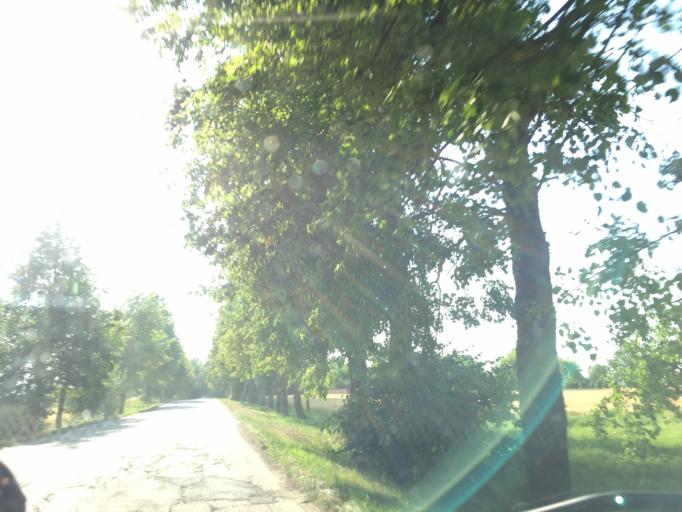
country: LV
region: Jelgava
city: Jelgava
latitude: 56.4504
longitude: 23.6844
